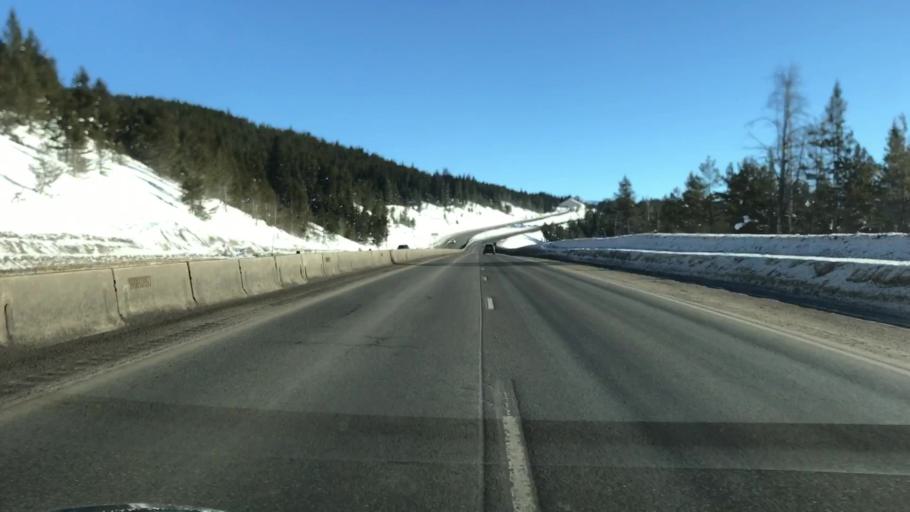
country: US
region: Colorado
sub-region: Summit County
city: Frisco
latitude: 39.5514
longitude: -106.2238
